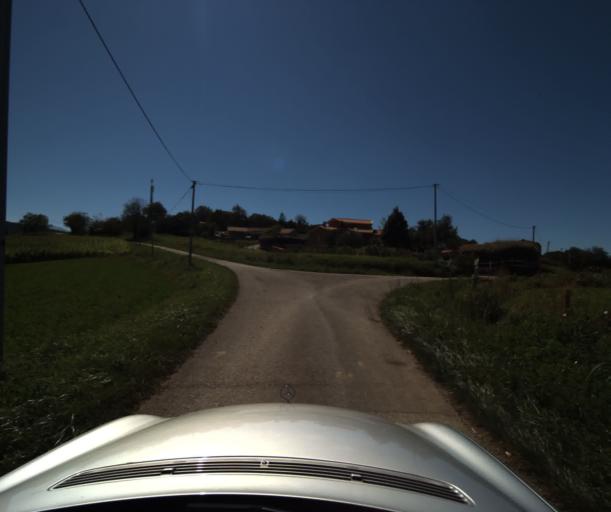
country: FR
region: Midi-Pyrenees
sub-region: Departement de l'Ariege
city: Belesta
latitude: 42.9618
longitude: 1.9339
